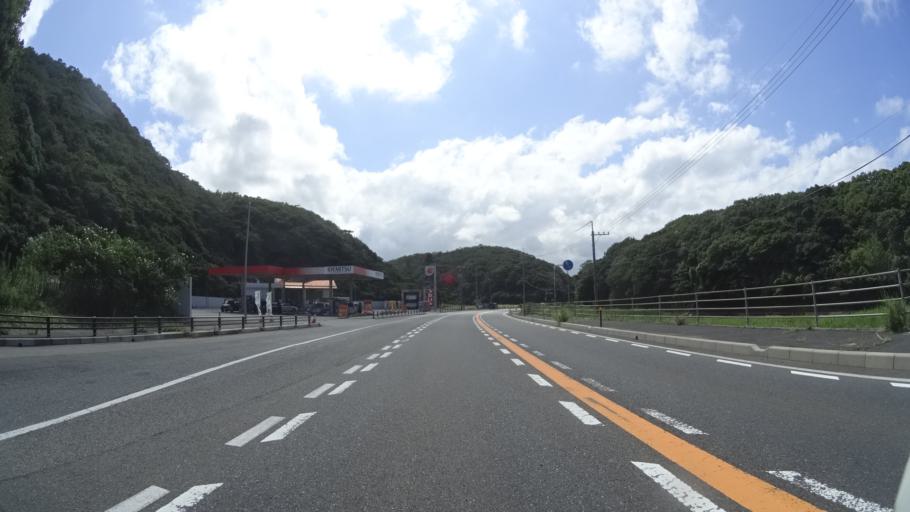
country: JP
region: Tottori
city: Tottori
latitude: 35.5230
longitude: 134.1082
